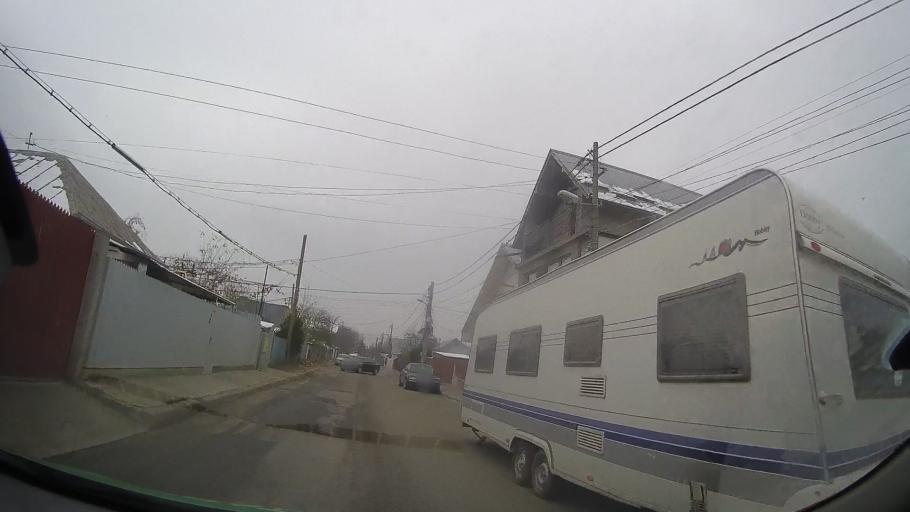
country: RO
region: Vaslui
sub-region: Municipiul Barlad
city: Barlad
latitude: 46.2358
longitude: 27.6788
